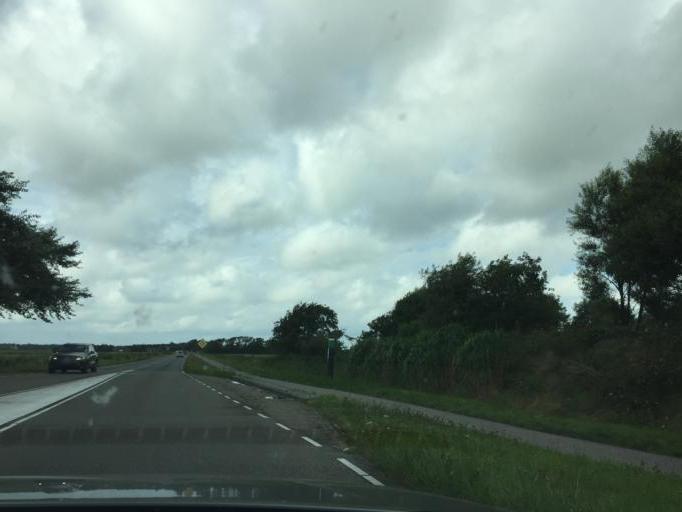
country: NL
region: North Holland
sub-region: Gemeente Texel
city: Den Burg
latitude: 53.0643
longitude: 4.7762
